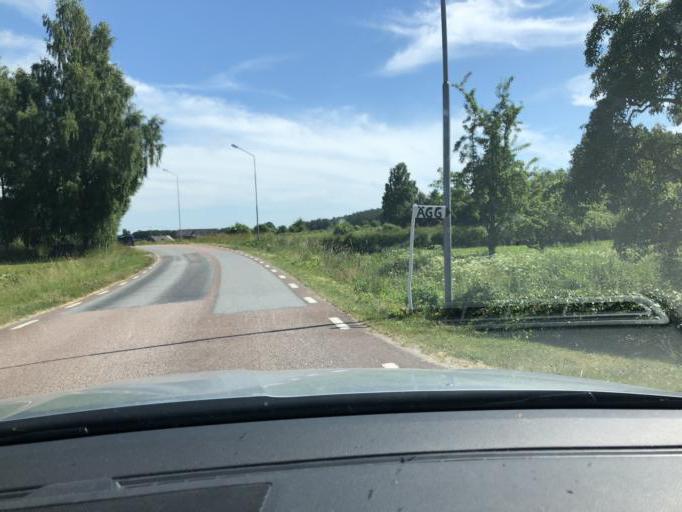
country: SE
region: Blekinge
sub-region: Solvesborgs Kommun
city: Soelvesborg
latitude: 56.1287
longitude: 14.6068
